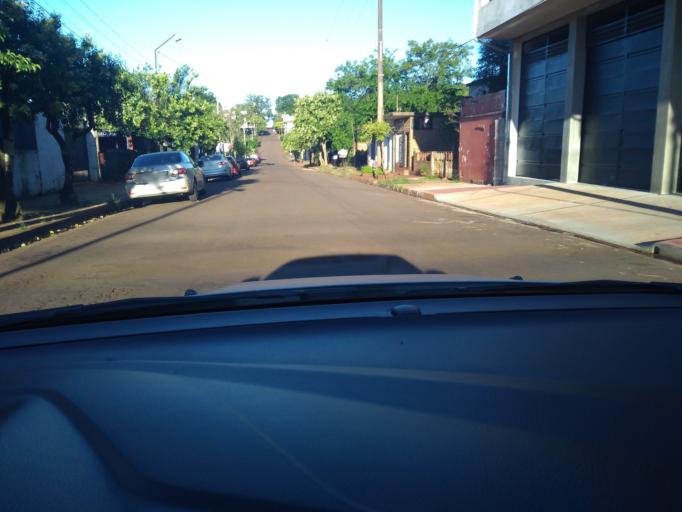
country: AR
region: Misiones
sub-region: Departamento de Obera
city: Obera
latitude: -27.4826
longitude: -55.1174
